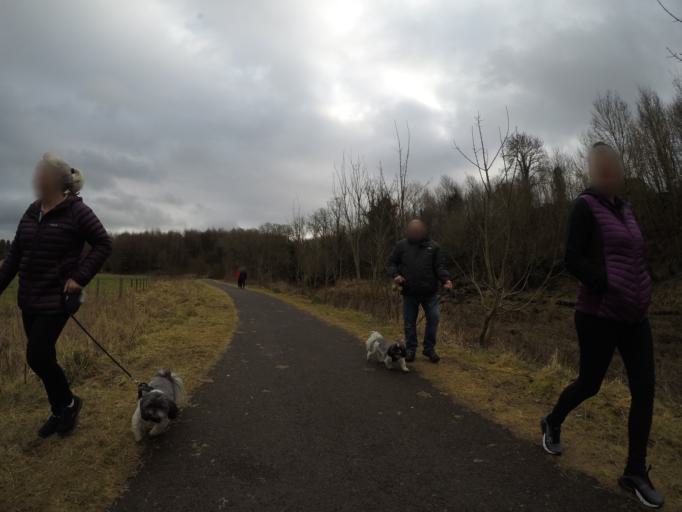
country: GB
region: Scotland
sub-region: North Ayrshire
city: Springside
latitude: 55.6127
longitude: -4.6111
